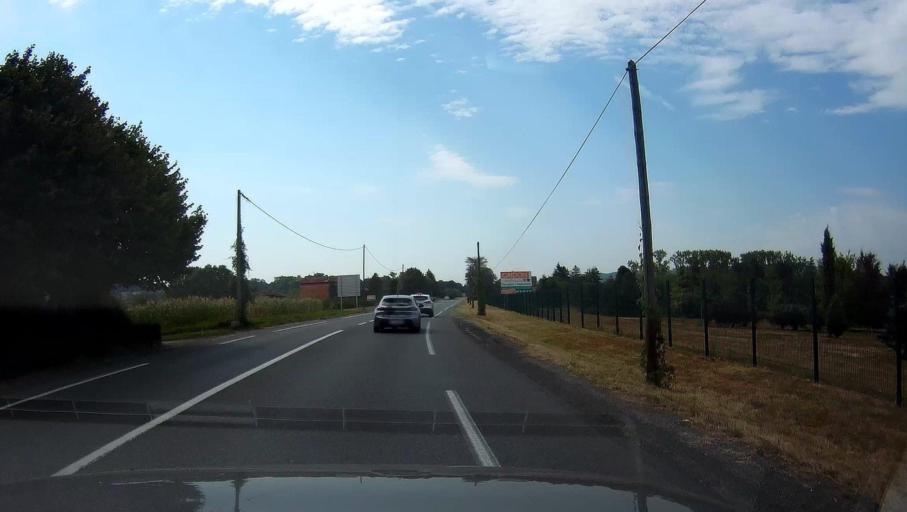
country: FR
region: Rhone-Alpes
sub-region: Departement de l'Ain
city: Reyrieux
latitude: 45.9202
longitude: 4.8144
